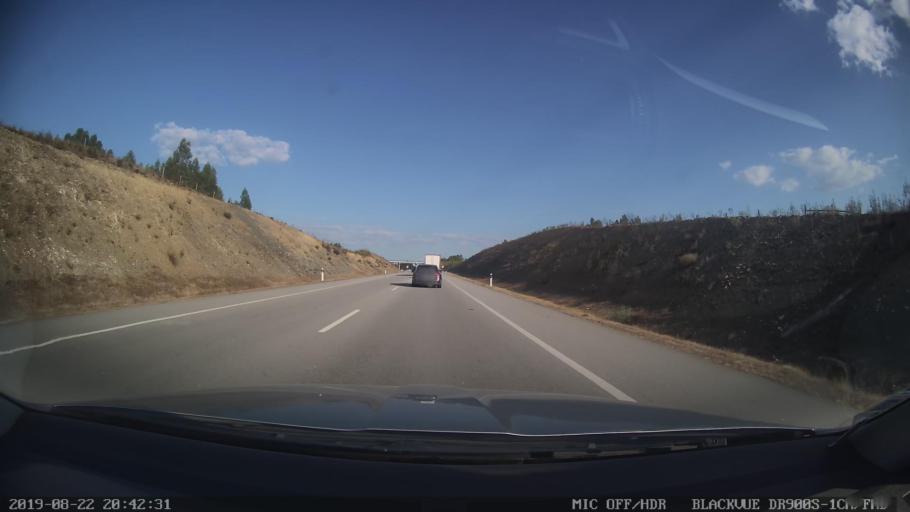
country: PT
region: Castelo Branco
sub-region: Proenca-A-Nova
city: Proenca-a-Nova
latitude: 39.6950
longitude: -7.8177
